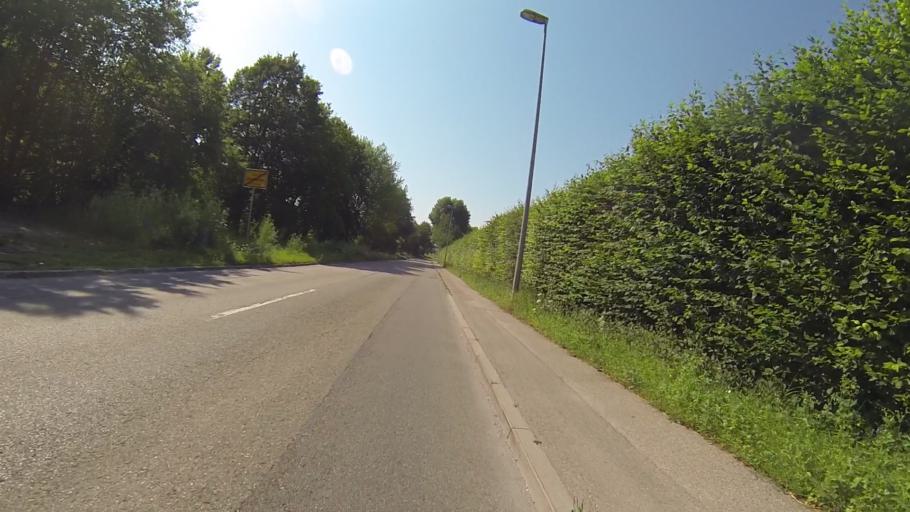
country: DE
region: Baden-Wuerttemberg
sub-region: Regierungsbezirk Stuttgart
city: Oberkochen
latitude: 48.7756
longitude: 10.0996
